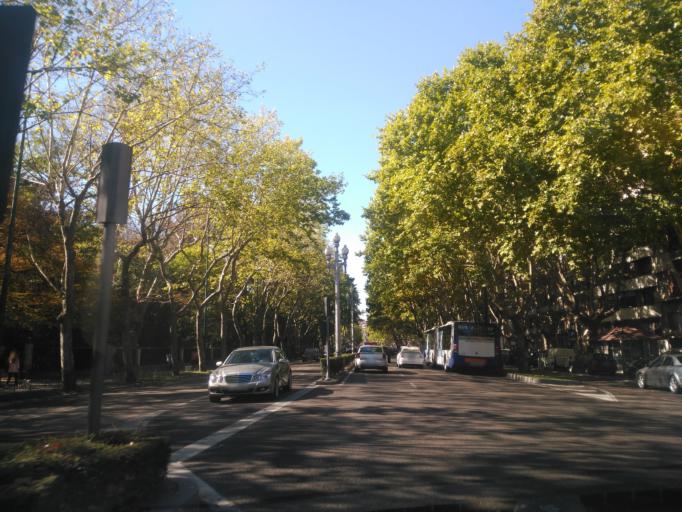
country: ES
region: Castille and Leon
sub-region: Provincia de Valladolid
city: Valladolid
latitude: 41.6465
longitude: -4.7319
